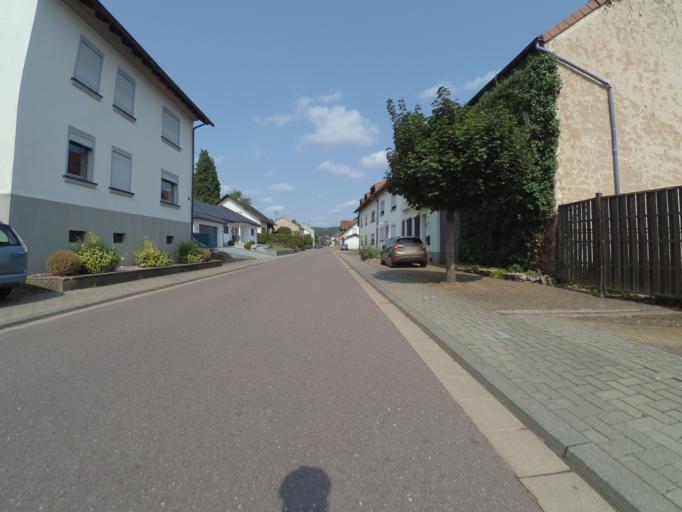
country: DE
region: Saarland
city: Merzig
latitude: 49.4665
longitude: 6.6749
